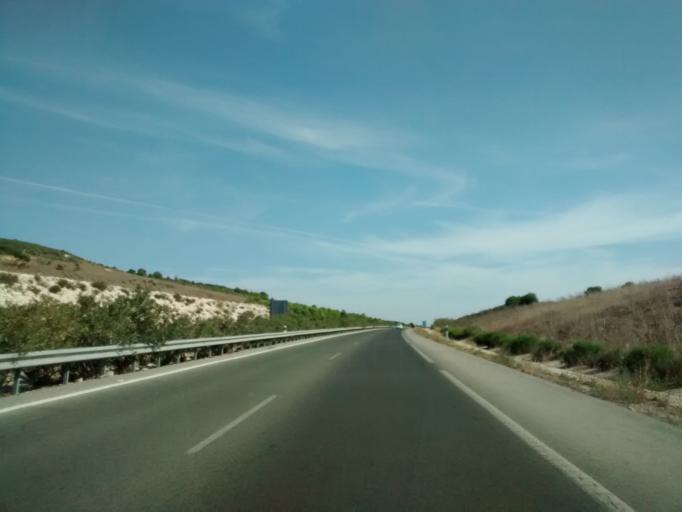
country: ES
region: Andalusia
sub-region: Provincia de Cadiz
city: Conil de la Frontera
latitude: 36.3209
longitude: -6.0567
